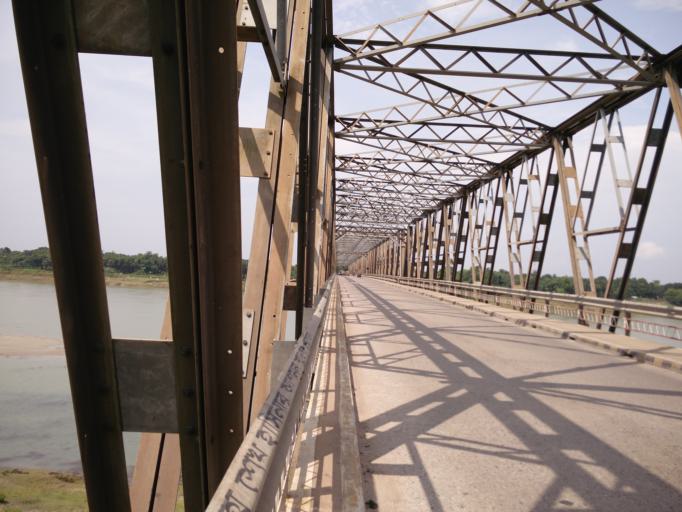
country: BD
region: Khulna
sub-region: Magura
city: Magura
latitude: 23.5438
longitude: 89.5179
